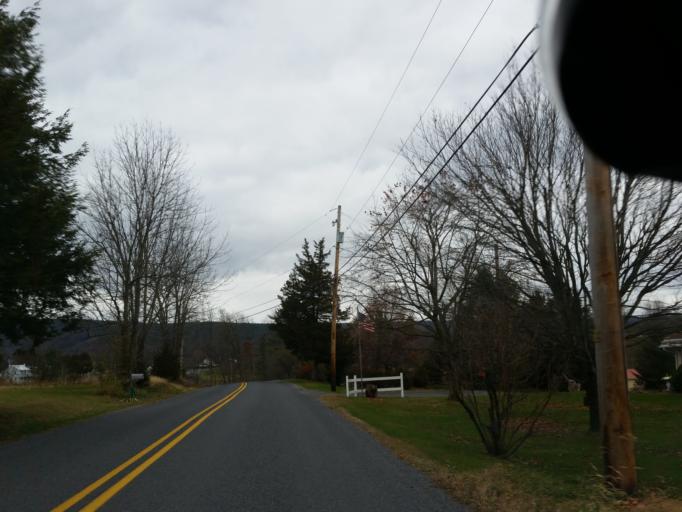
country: US
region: Pennsylvania
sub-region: Union County
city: New Columbia
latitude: 41.0343
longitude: -76.9447
